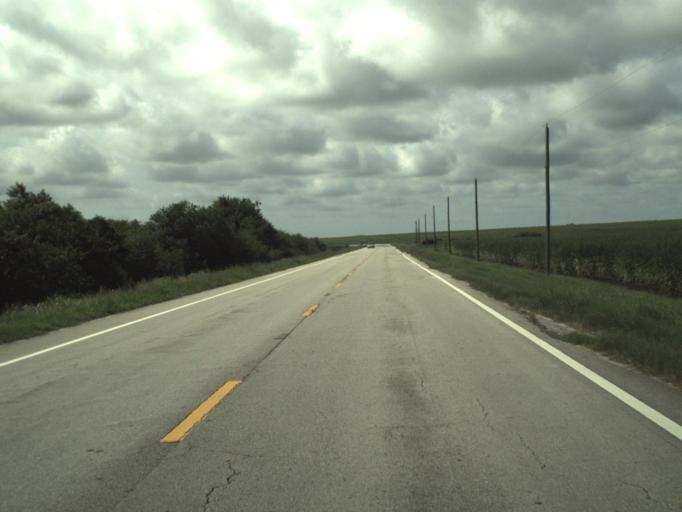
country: US
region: Florida
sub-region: Palm Beach County
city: Pahokee
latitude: 26.7730
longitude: -80.6891
